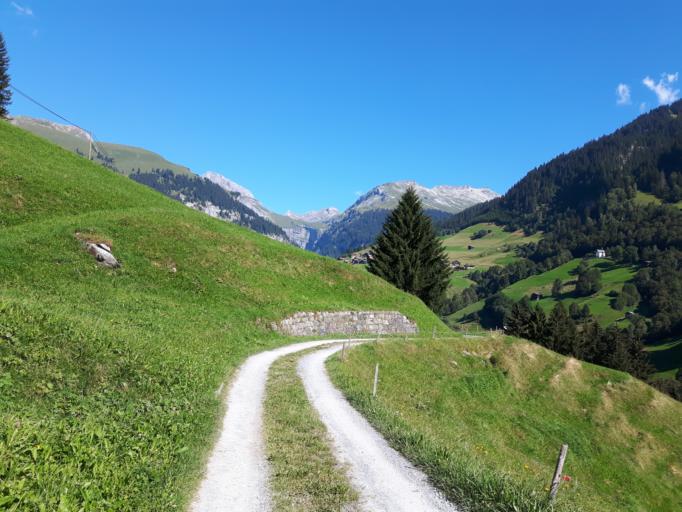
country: CH
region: Grisons
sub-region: Surselva District
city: Breil
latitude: 46.7994
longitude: 9.1183
